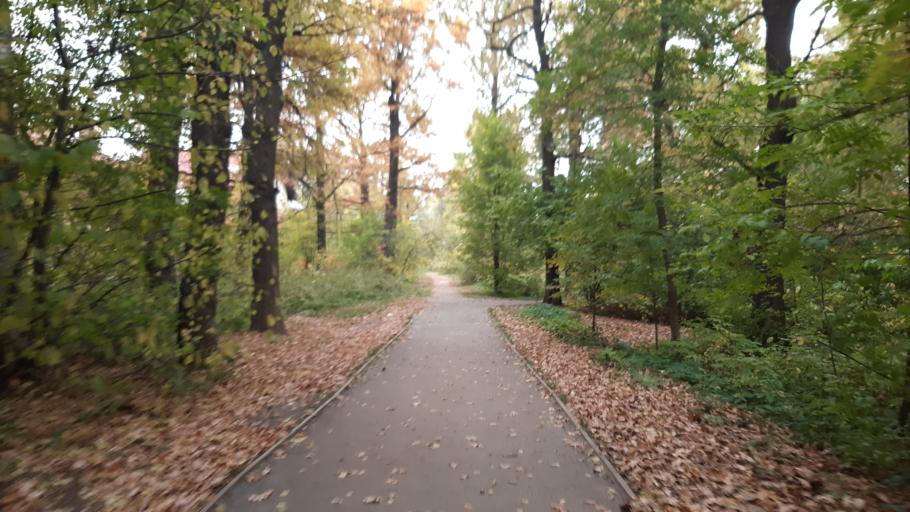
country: RU
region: Moscow
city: Vagonoremont
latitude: 55.9046
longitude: 37.5660
